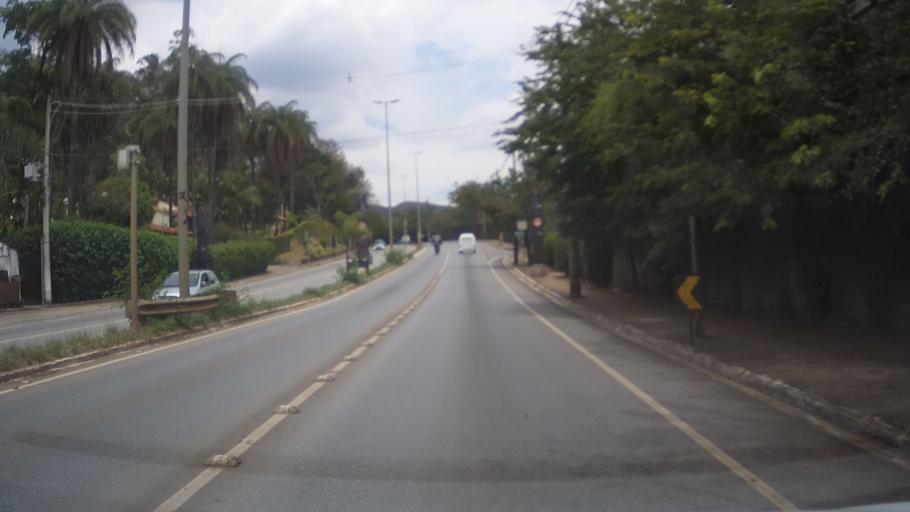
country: BR
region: Minas Gerais
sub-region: Nova Lima
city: Nova Lima
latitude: -19.9991
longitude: -43.8971
